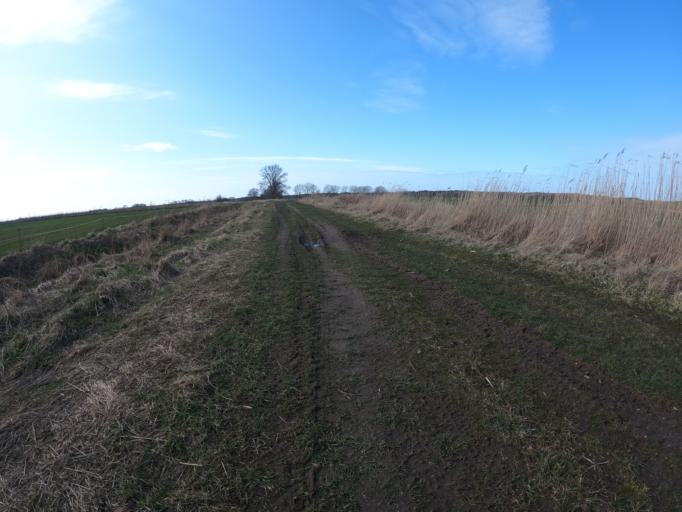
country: PL
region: West Pomeranian Voivodeship
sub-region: Powiat gryficki
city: Trzebiatow
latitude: 54.0950
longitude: 15.1942
